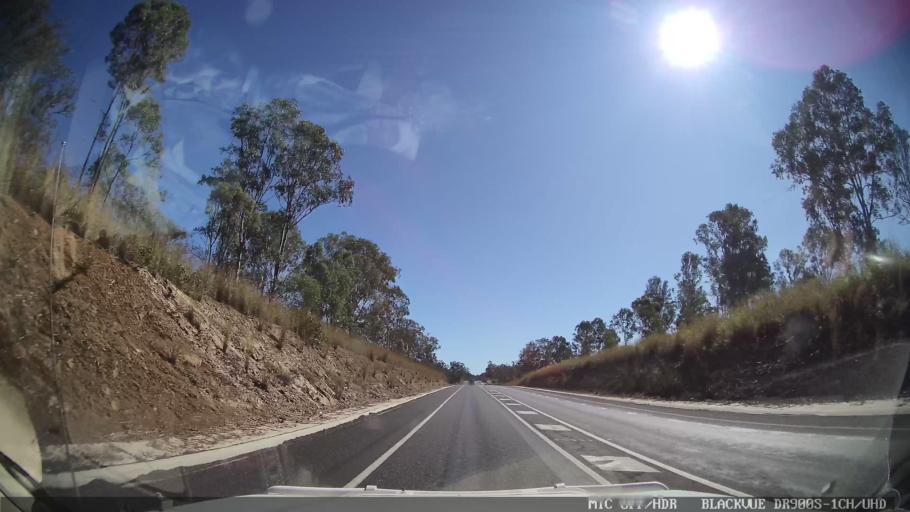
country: AU
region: Queensland
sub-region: Gympie Regional Council
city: Gympie
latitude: -26.0373
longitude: 152.5691
